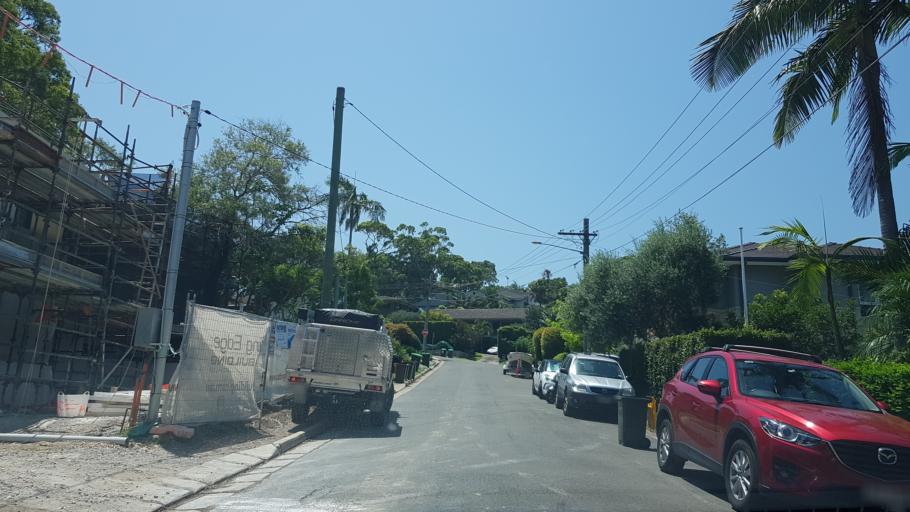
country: AU
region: New South Wales
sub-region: Pittwater
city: Bay View
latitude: -33.6551
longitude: 151.3056
